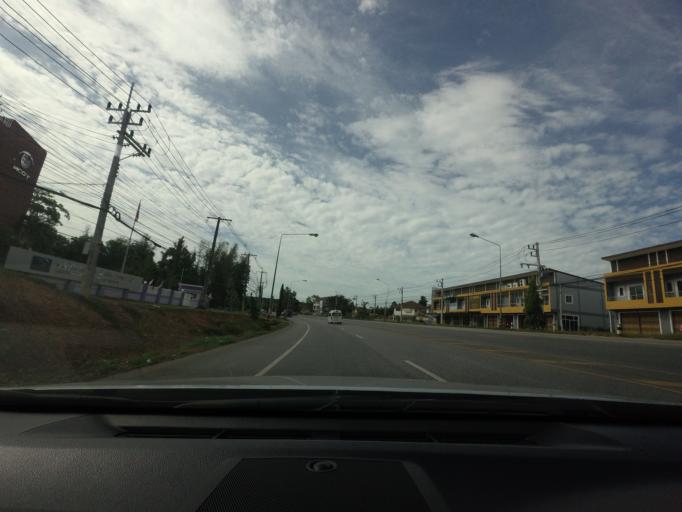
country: TH
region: Songkhla
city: Hat Yai
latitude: 6.9698
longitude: 100.4291
